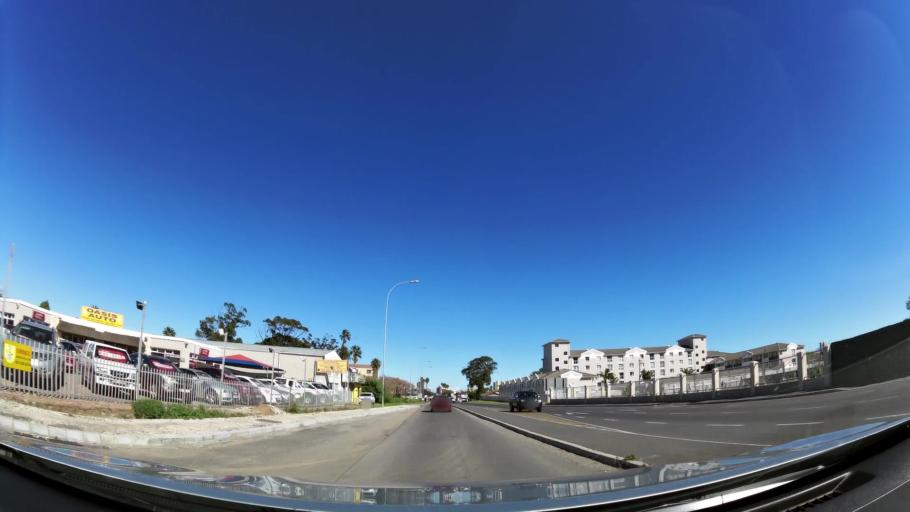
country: ZA
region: Western Cape
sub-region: Cape Winelands District Municipality
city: Stellenbosch
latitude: -34.1081
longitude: 18.8382
